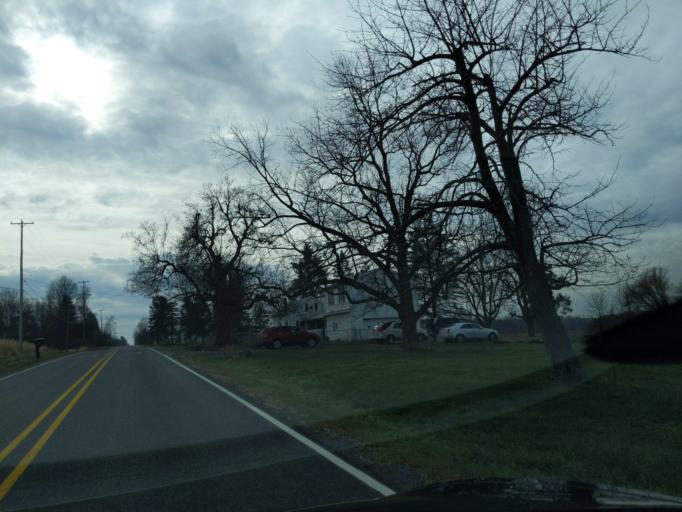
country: US
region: Michigan
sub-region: Ingham County
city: Mason
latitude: 42.5200
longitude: -84.5224
